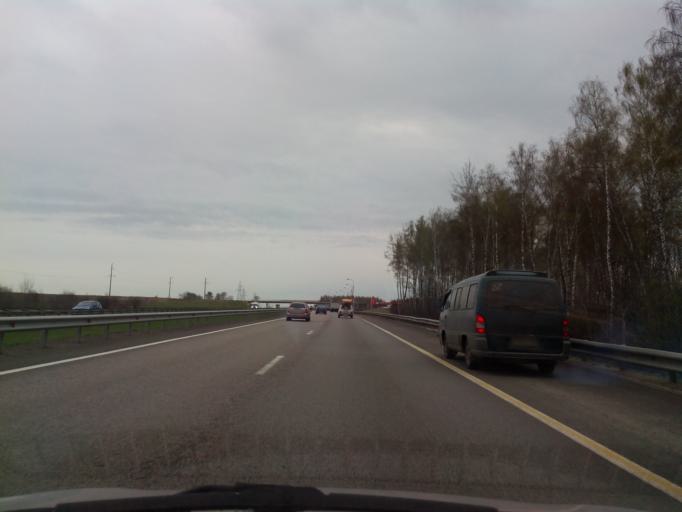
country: RU
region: Moskovskaya
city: Kashira
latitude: 54.7910
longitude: 38.1002
